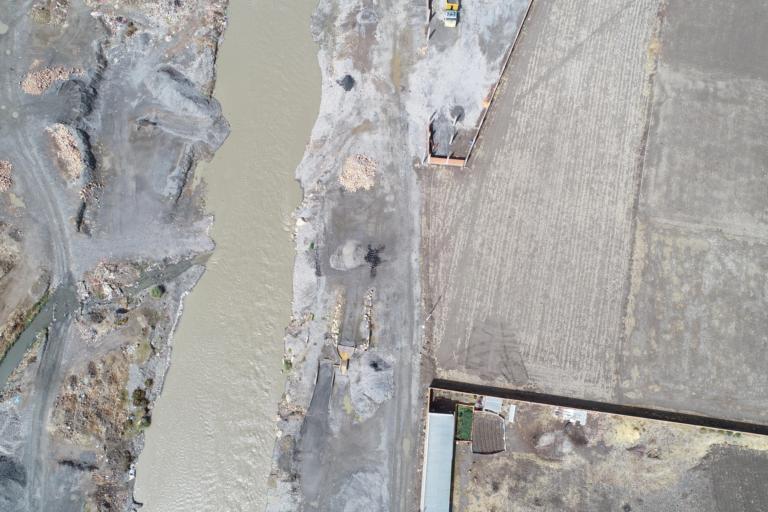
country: BO
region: La Paz
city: Achacachi
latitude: -16.0383
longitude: -68.6891
